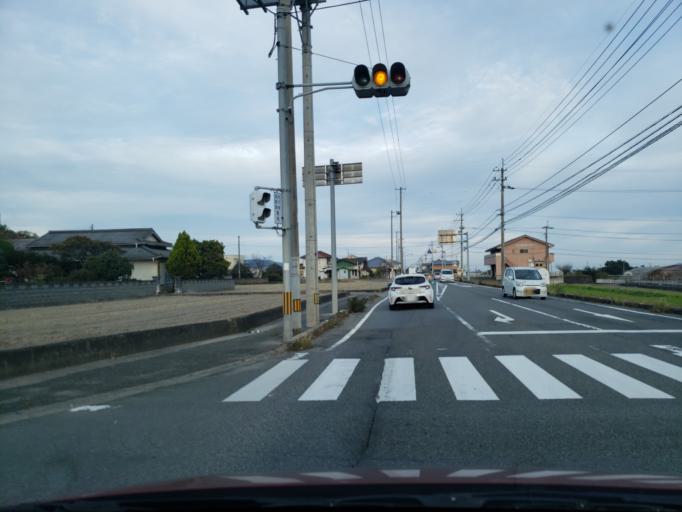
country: JP
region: Tokushima
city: Kamojimacho-jogejima
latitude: 34.0874
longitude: 134.2934
